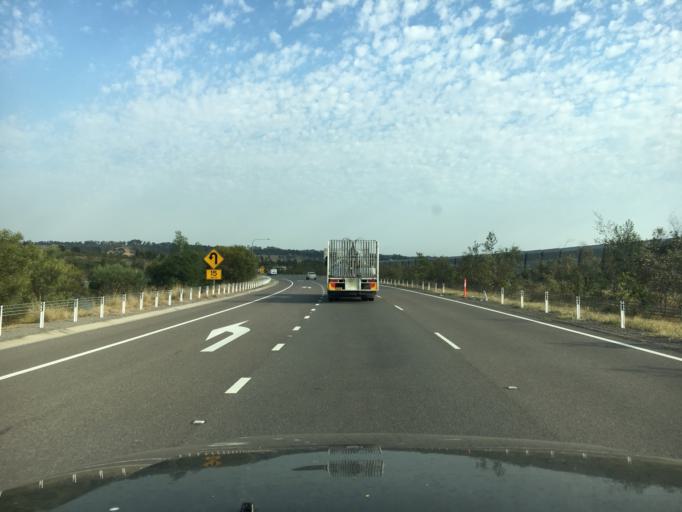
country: AU
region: New South Wales
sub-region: Cessnock
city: Branxton
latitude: -32.6585
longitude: 151.3392
